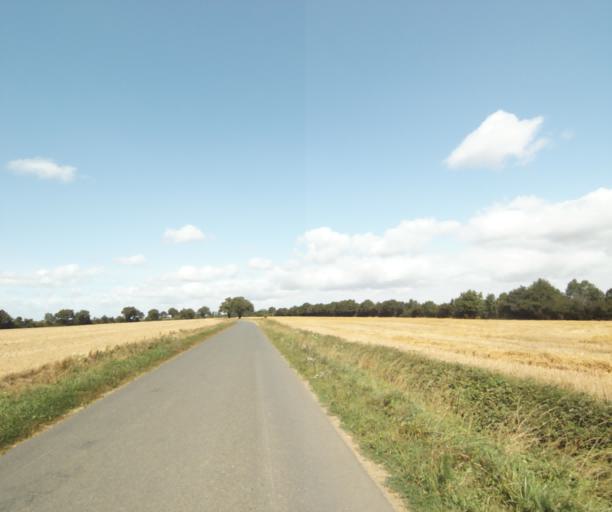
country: FR
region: Pays de la Loire
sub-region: Departement de la Sarthe
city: Sable-sur-Sarthe
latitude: 47.8482
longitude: -0.3856
